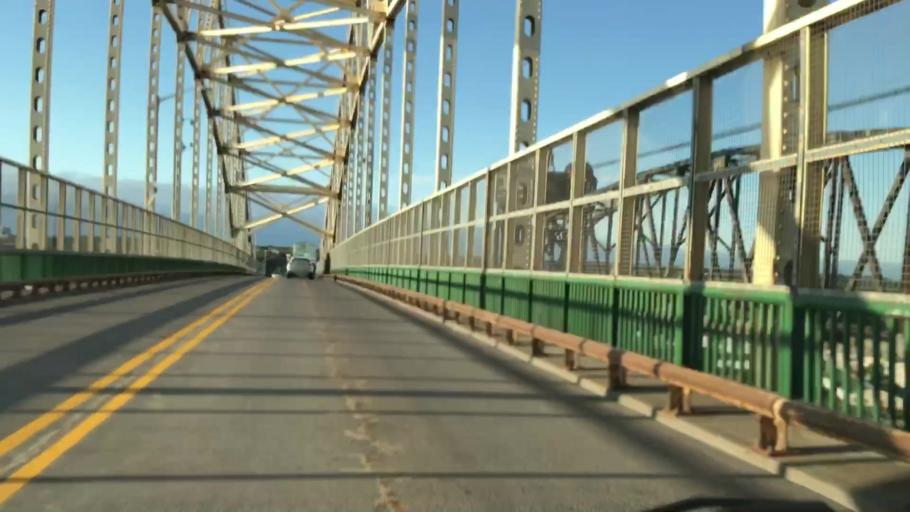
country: US
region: Michigan
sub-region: Chippewa County
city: Sault Ste. Marie
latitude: 46.5028
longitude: -84.3631
